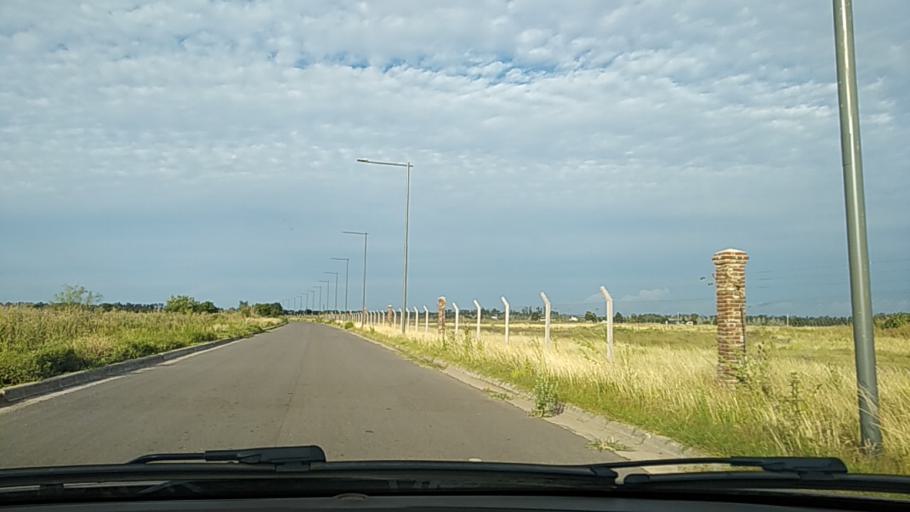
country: AR
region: Santa Fe
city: Funes
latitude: -32.9442
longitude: -60.7763
